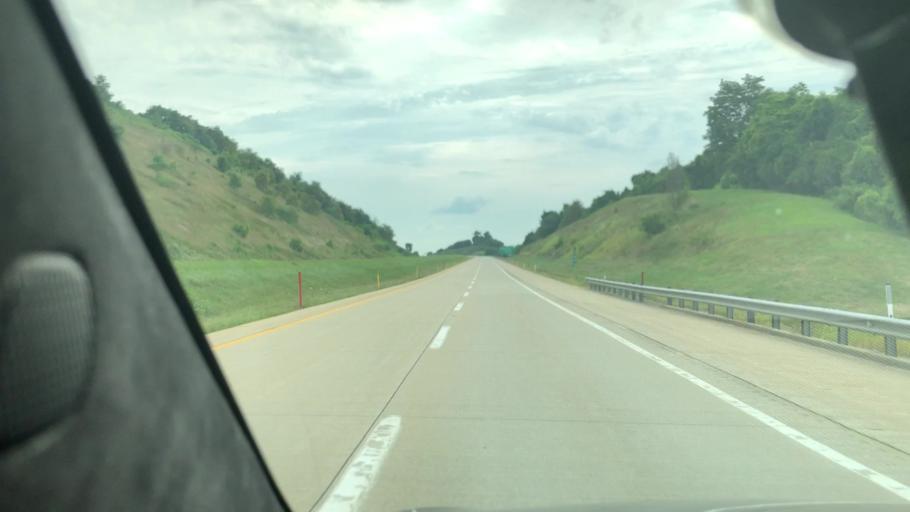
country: US
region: Pennsylvania
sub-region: Washington County
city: Gastonville
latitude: 40.2696
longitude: -79.9665
